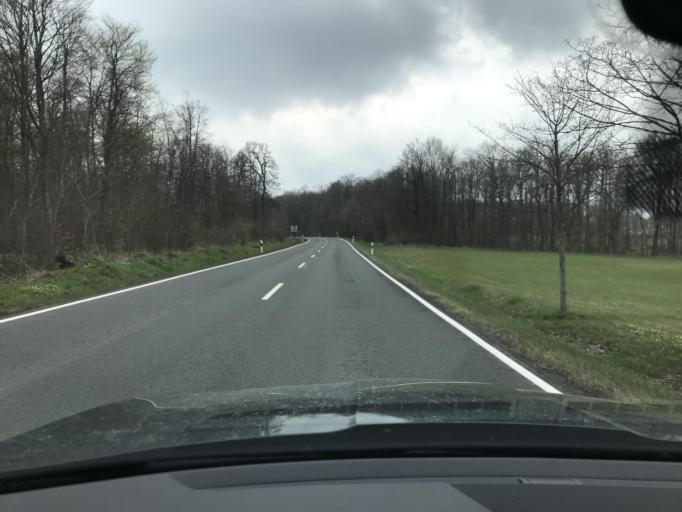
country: DE
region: Saxony-Anhalt
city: Harzgerode
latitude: 51.6199
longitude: 11.1581
